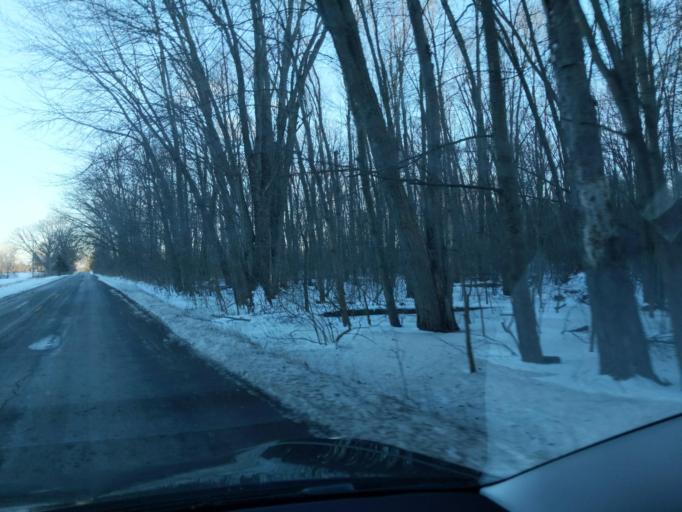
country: US
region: Michigan
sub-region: Ingham County
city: Stockbridge
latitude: 42.4613
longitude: -84.2375
